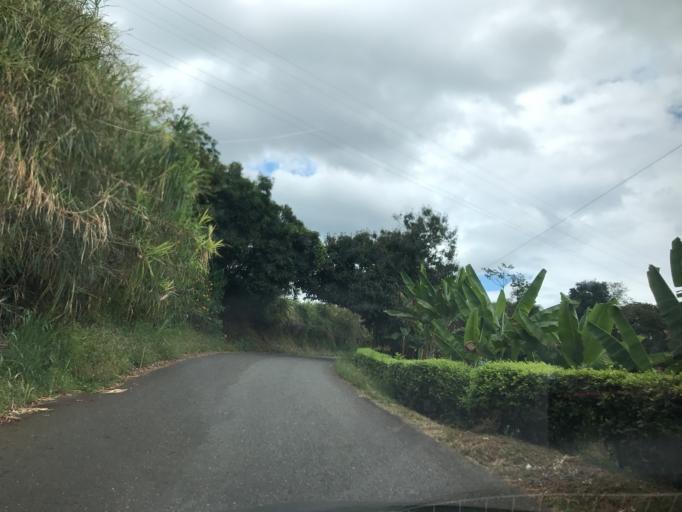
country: CO
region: Quindio
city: Buenavista
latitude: 4.3688
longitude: -75.7540
